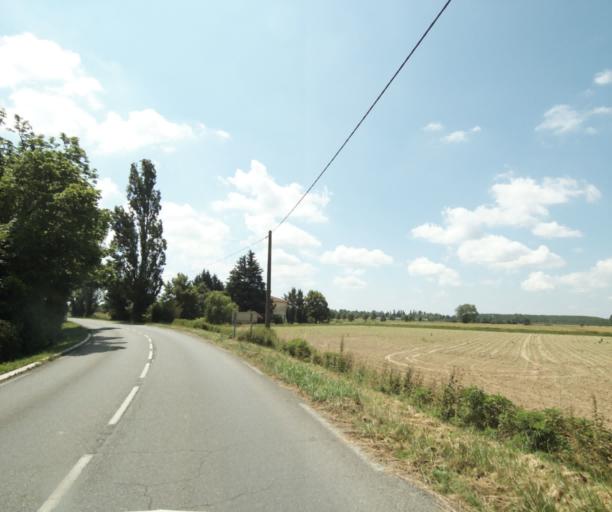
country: FR
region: Midi-Pyrenees
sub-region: Departement du Tarn-et-Garonne
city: Montauban
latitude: 44.0827
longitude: 1.3468
